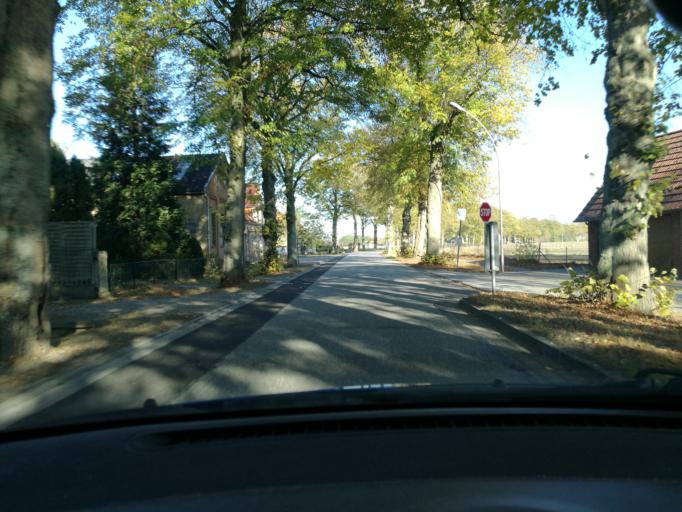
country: DE
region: Brandenburg
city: Lanz
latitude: 53.1504
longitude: 11.5787
